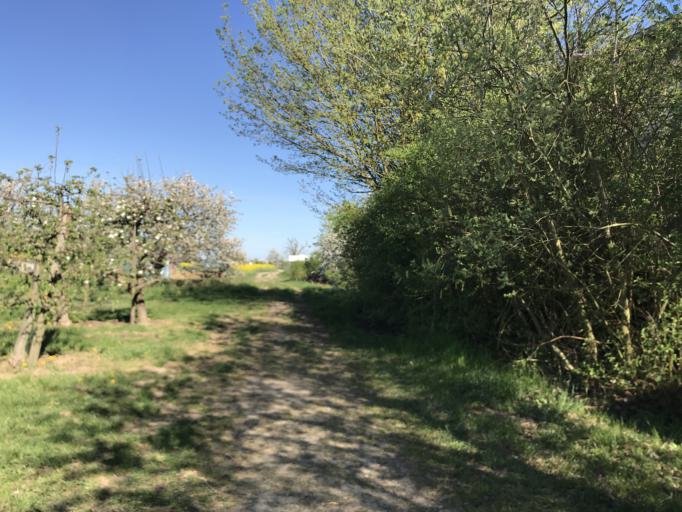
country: DE
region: Rheinland-Pfalz
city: Wackernheim
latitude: 49.9723
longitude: 8.1247
